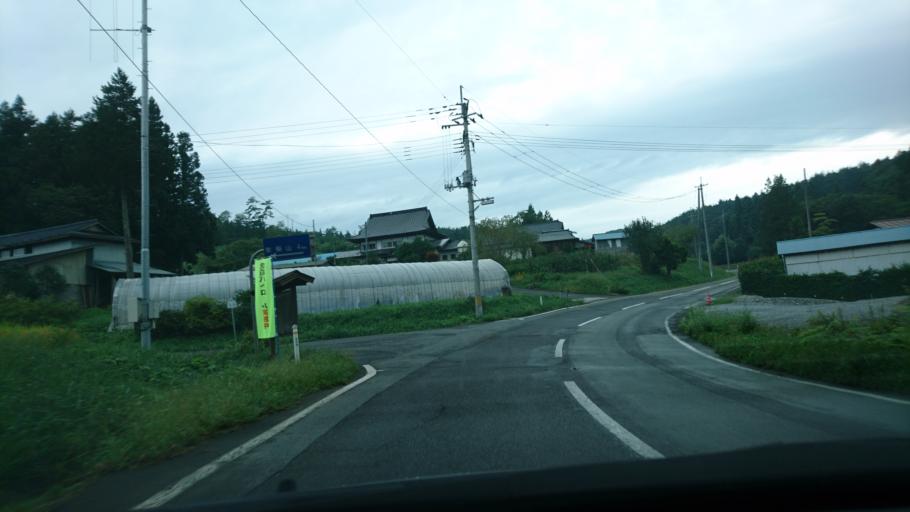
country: JP
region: Iwate
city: Mizusawa
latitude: 39.0287
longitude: 141.2023
